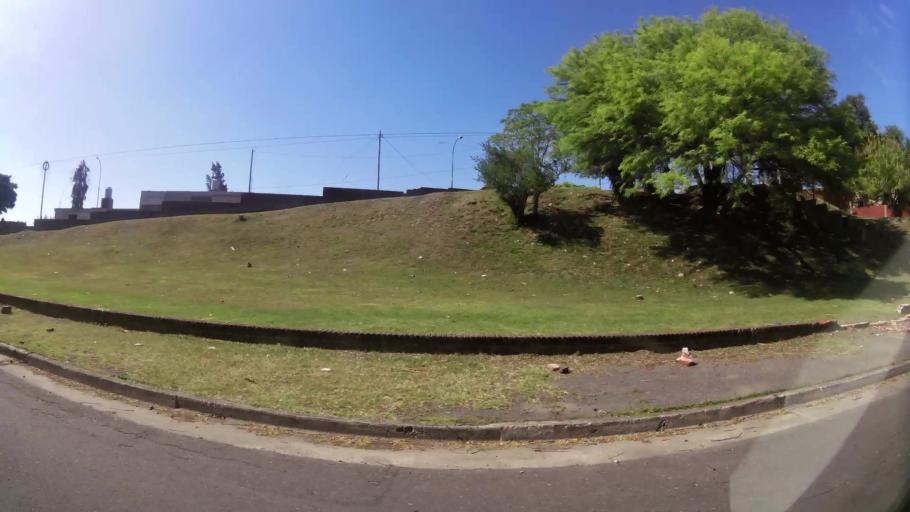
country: AR
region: Cordoba
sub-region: Departamento de Capital
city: Cordoba
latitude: -31.4158
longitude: -64.1557
